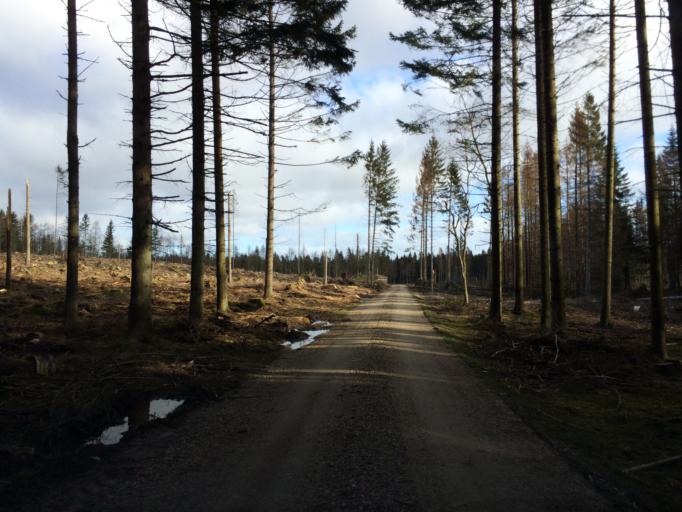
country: DK
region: Central Jutland
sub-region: Holstebro Kommune
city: Ulfborg
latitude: 56.2691
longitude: 8.4464
